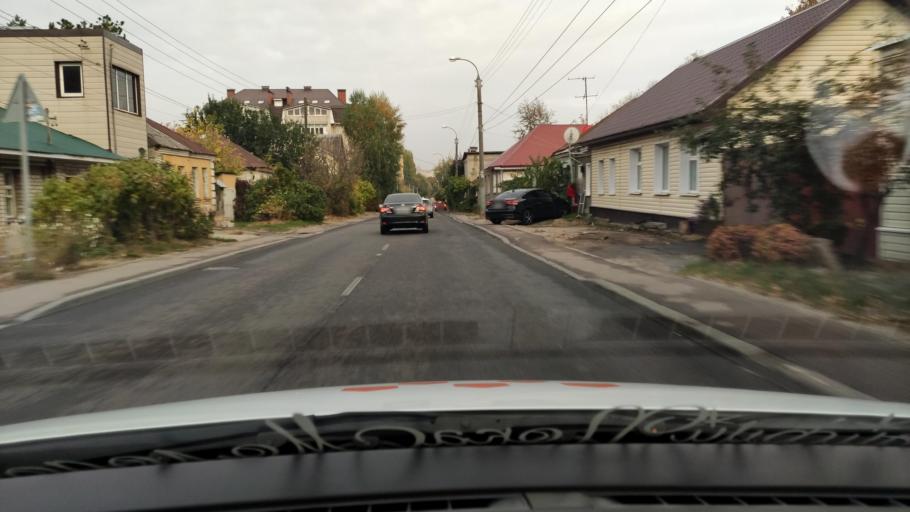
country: RU
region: Voronezj
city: Voronezh
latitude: 51.6525
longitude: 39.2043
